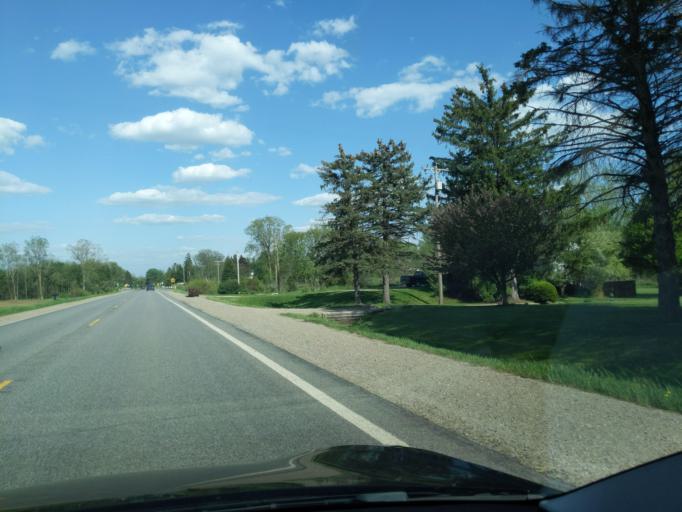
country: US
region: Michigan
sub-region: Eaton County
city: Grand Ledge
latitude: 42.7555
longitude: -84.7834
